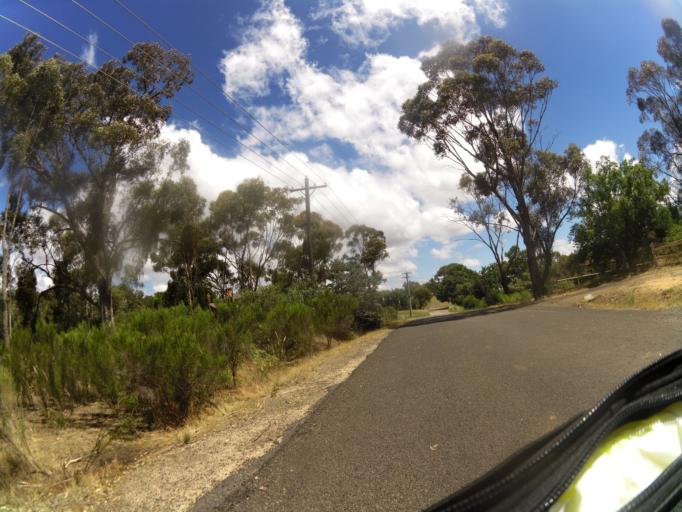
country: AU
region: Victoria
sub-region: Mount Alexander
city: Castlemaine
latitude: -37.0035
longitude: 144.2530
